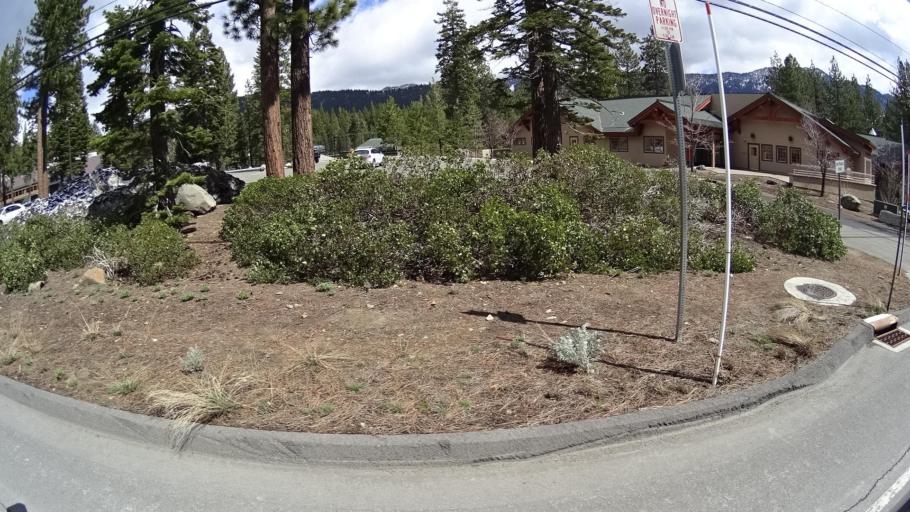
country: US
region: Nevada
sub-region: Washoe County
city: Incline Village
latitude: 39.2456
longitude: -119.9468
